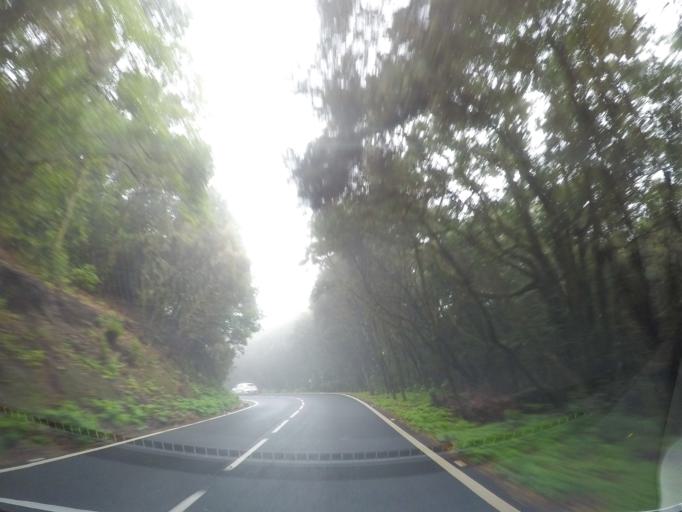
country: ES
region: Canary Islands
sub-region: Provincia de Santa Cruz de Tenerife
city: Vallehermosa
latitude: 28.1425
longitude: -17.2850
